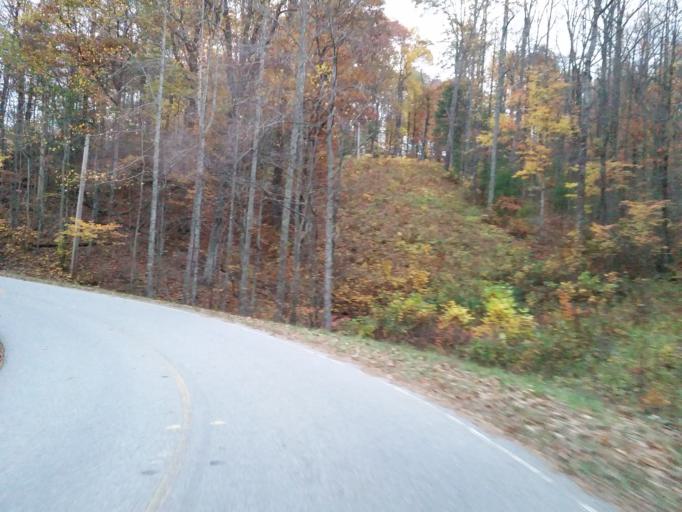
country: US
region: Georgia
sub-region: Lumpkin County
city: Dahlonega
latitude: 34.7008
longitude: -84.0326
